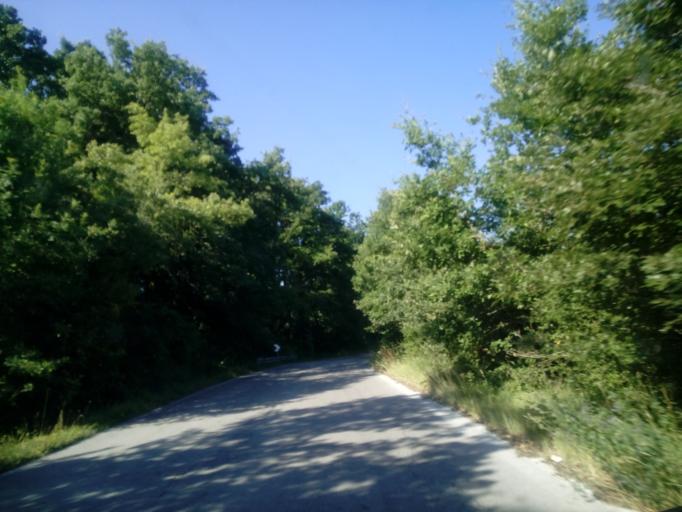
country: IT
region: Molise
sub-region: Provincia di Campobasso
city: Jelsi
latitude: 41.5106
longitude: 14.7779
